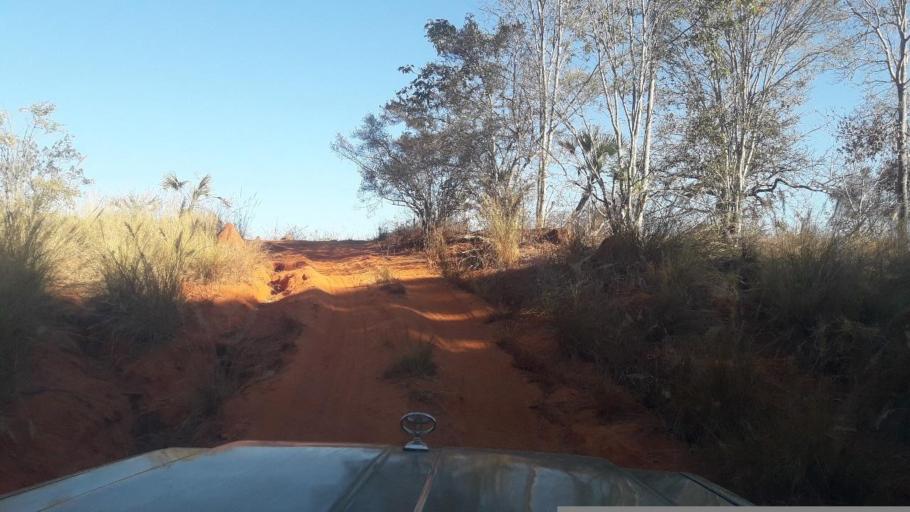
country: MG
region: Boeny
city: Sitampiky
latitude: -16.4067
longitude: 45.5993
